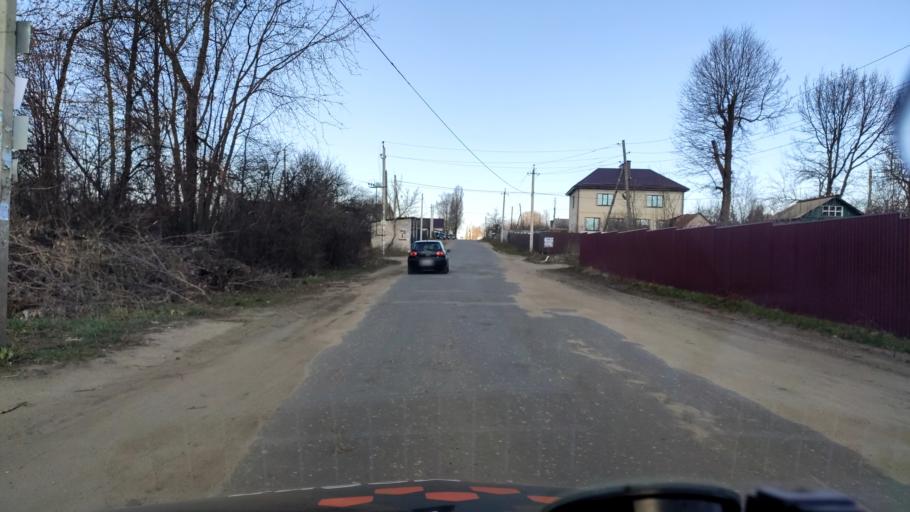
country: RU
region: Voronezj
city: Shilovo
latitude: 51.5960
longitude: 39.1511
